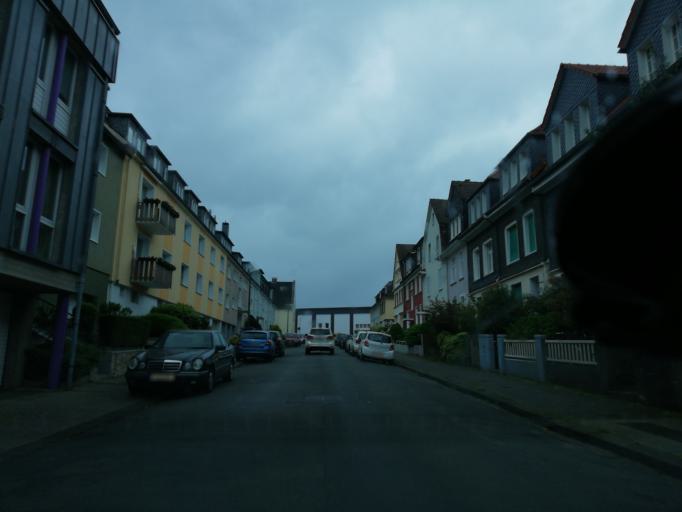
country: DE
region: North Rhine-Westphalia
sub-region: Regierungsbezirk Dusseldorf
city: Solingen
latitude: 51.2360
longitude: 7.0837
